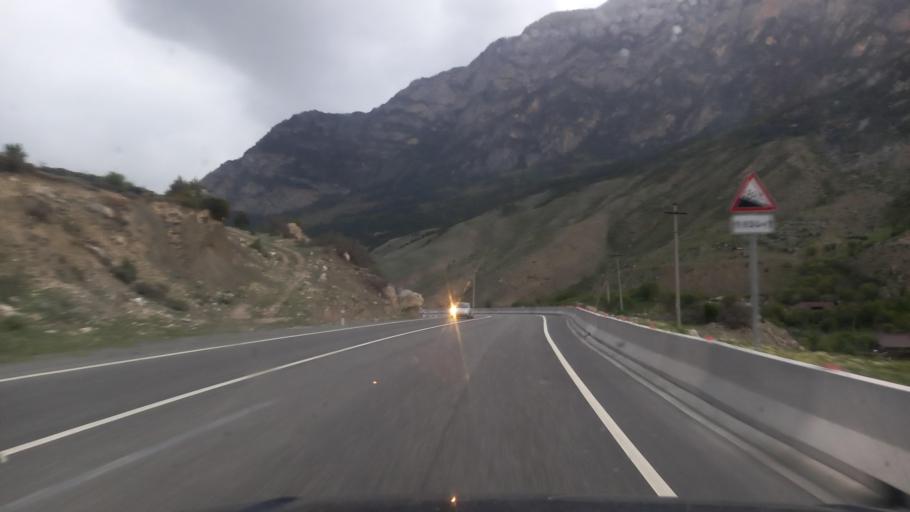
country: RU
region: North Ossetia
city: Mizur
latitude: 42.8828
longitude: 44.1627
